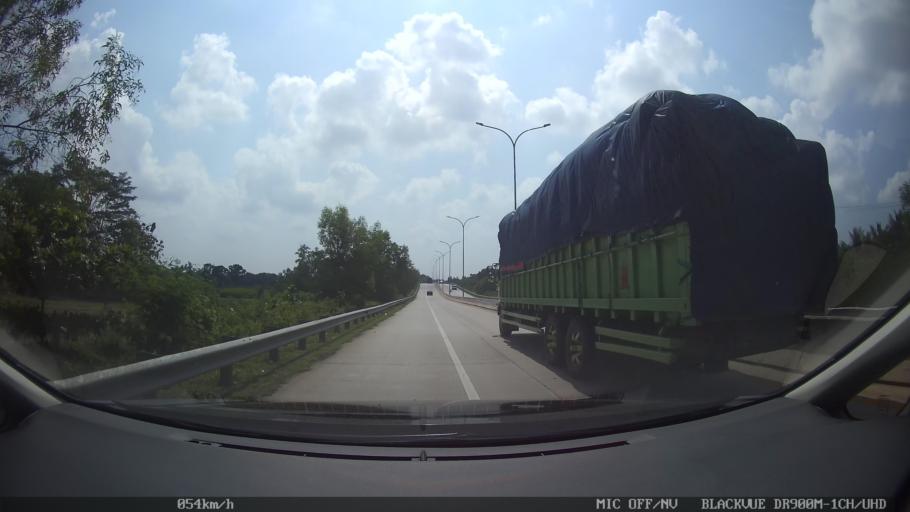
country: ID
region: Lampung
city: Natar
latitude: -5.2811
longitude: 105.1956
